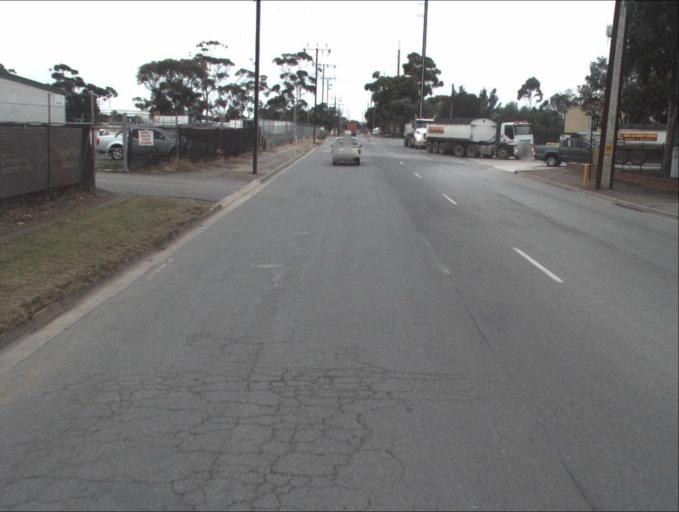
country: AU
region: South Australia
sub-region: Port Adelaide Enfield
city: Enfield
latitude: -34.8337
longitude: 138.5916
